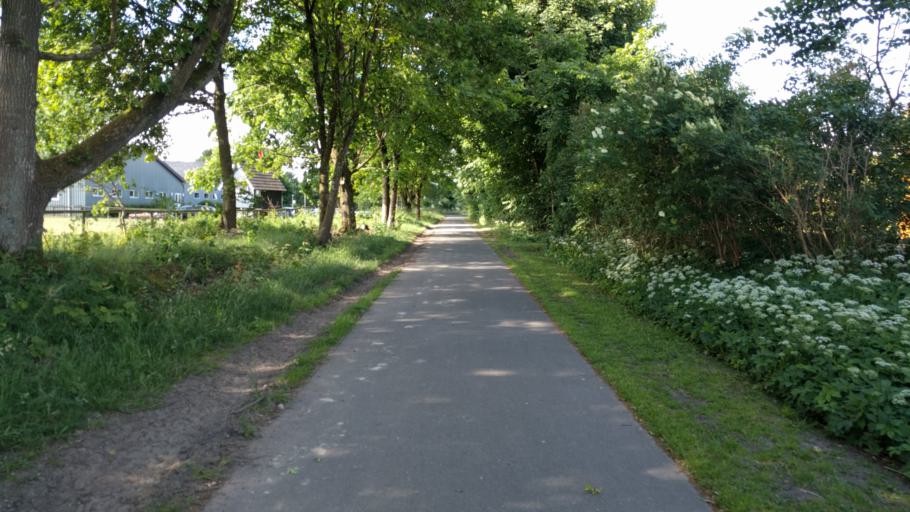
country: DK
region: Central Jutland
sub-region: Viborg Kommune
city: Viborg
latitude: 56.4238
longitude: 9.3829
